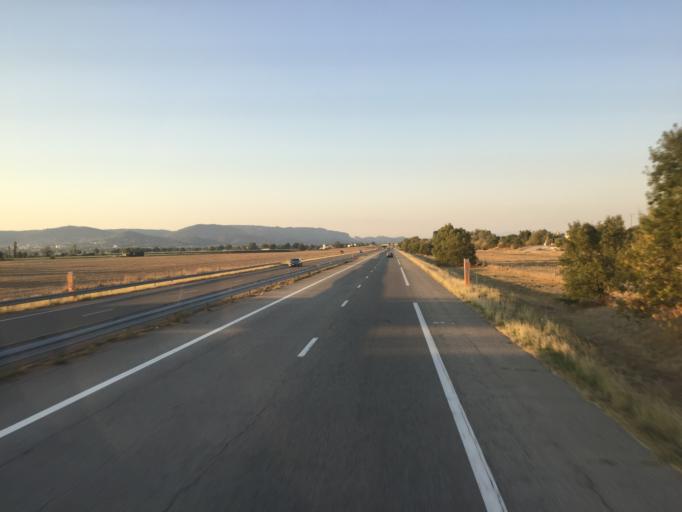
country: FR
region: Provence-Alpes-Cote d'Azur
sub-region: Departement des Alpes-de-Haute-Provence
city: Sainte-Tulle
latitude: 43.7815
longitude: 5.8036
